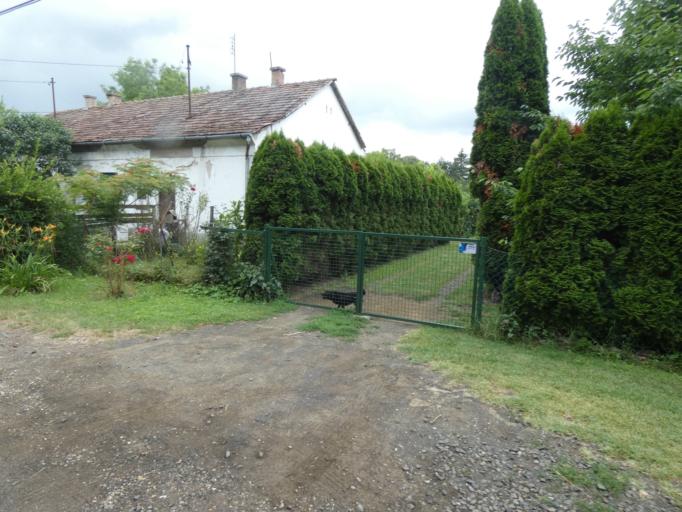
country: HU
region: Pest
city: Szob
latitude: 47.8118
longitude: 18.9017
